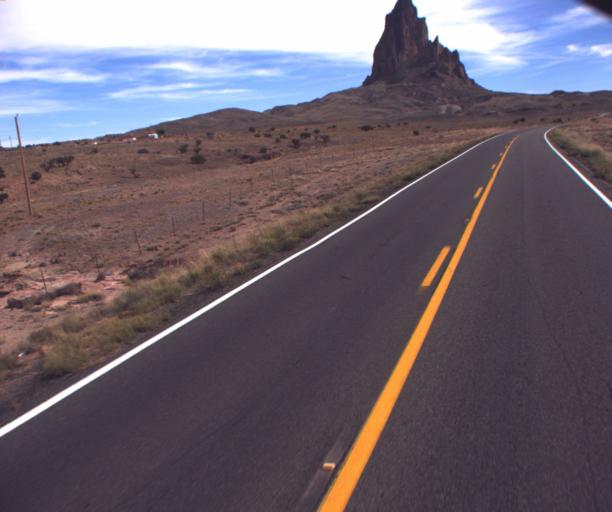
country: US
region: Arizona
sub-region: Navajo County
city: Kayenta
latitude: 36.8343
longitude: -110.2489
